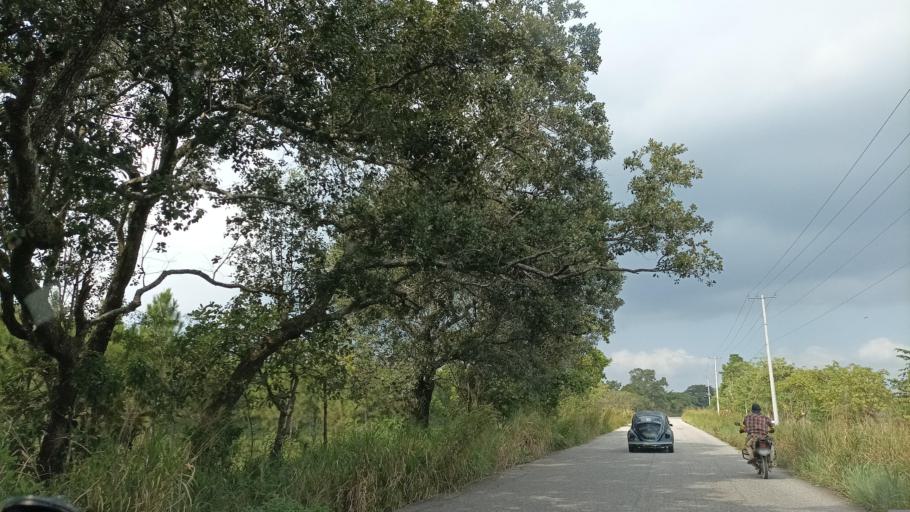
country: MX
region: Veracruz
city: Las Choapas
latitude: 17.8203
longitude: -94.1092
